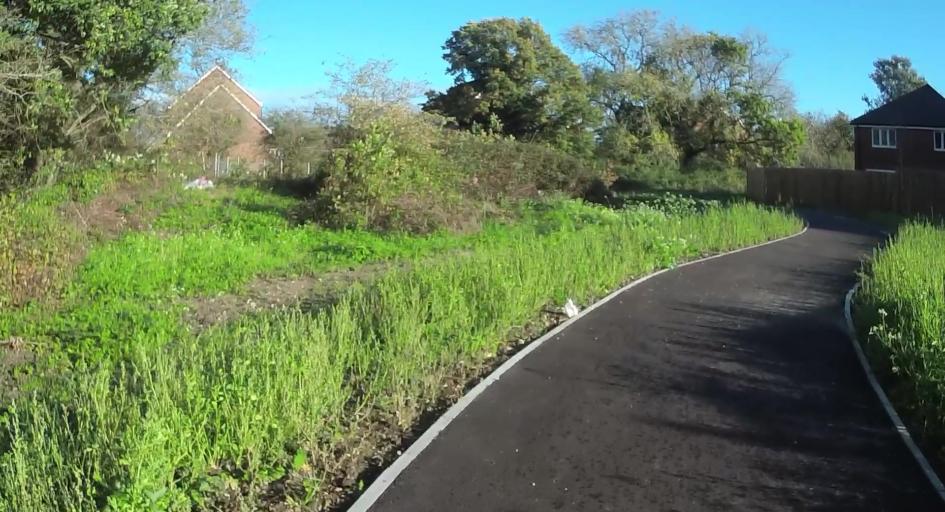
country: GB
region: England
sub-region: Wokingham
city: Winnersh
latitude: 51.4299
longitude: -0.8882
